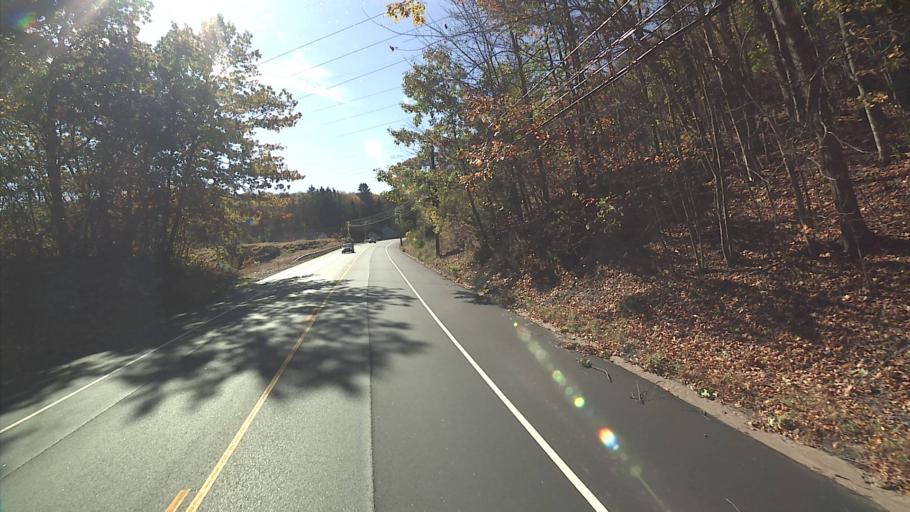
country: US
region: Connecticut
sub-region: Litchfield County
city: Watertown
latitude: 41.6281
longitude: -73.1026
